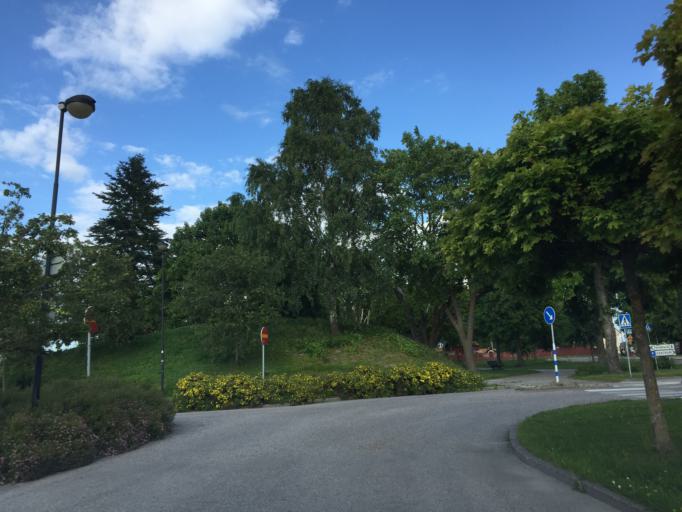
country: SE
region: Vaestmanland
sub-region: Arboga Kommun
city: Arboga
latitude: 59.3965
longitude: 15.8418
